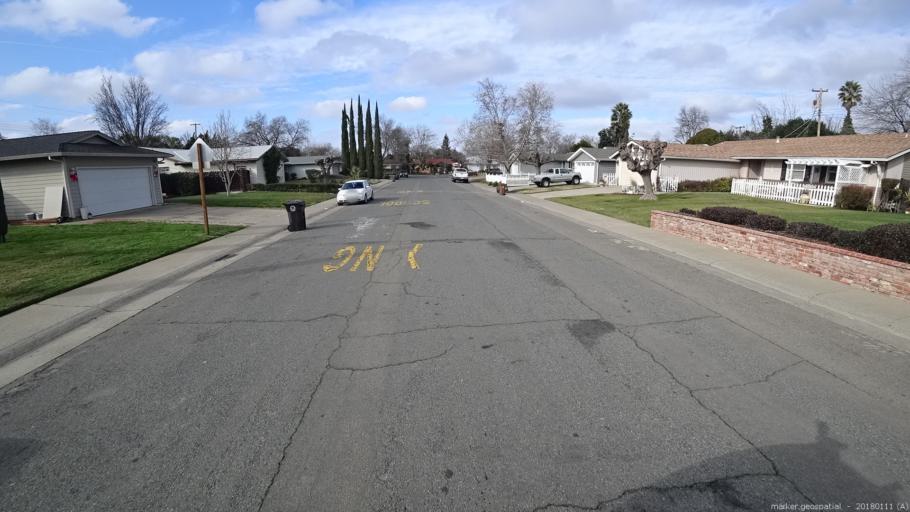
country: US
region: California
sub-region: Sacramento County
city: Rancho Cordova
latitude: 38.6075
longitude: -121.3017
